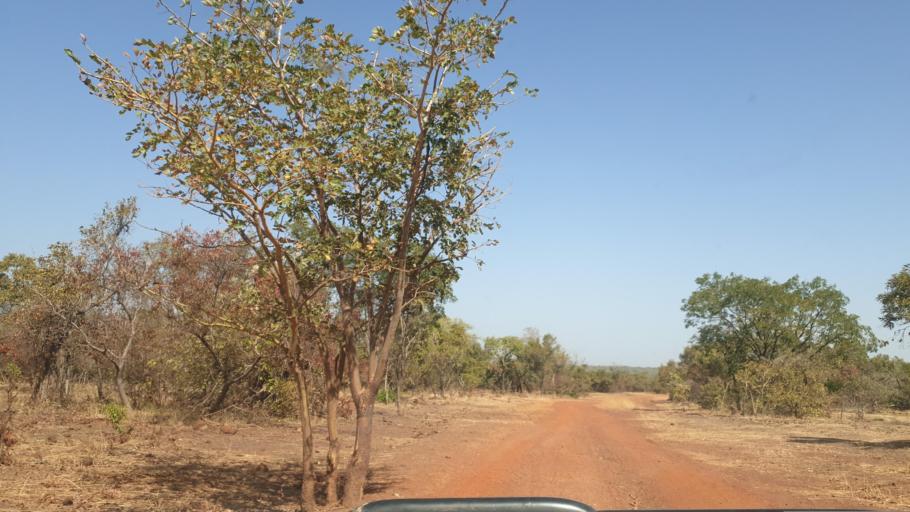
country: ML
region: Koulikoro
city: Dioila
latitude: 11.9165
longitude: -6.9845
